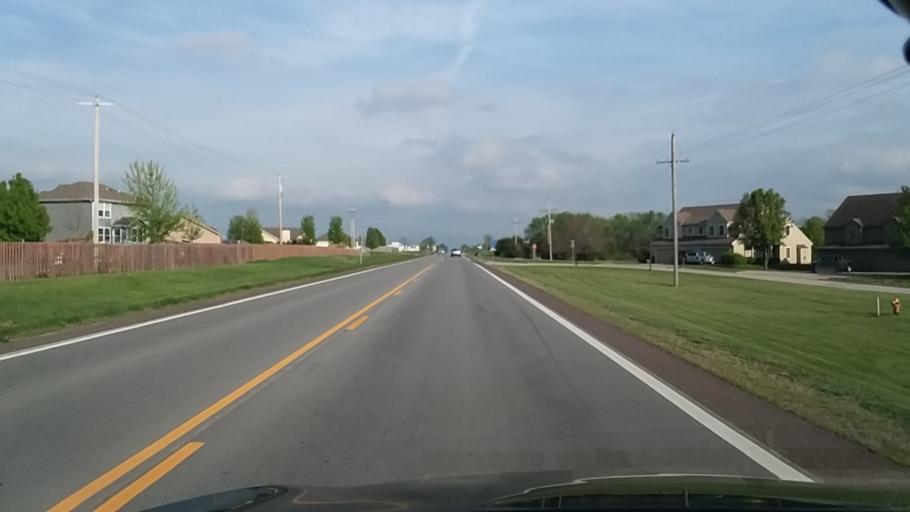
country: US
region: Kansas
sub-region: Douglas County
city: Baldwin City
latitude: 38.7771
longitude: -95.1706
